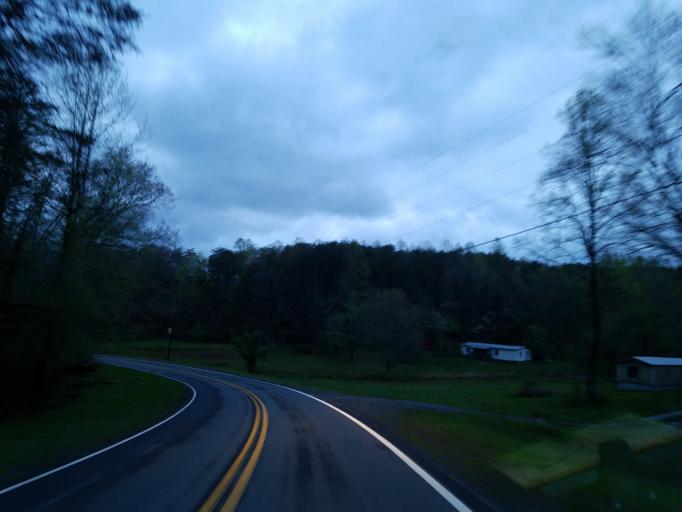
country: US
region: Georgia
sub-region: Fannin County
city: Blue Ridge
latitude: 34.6886
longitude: -84.2996
